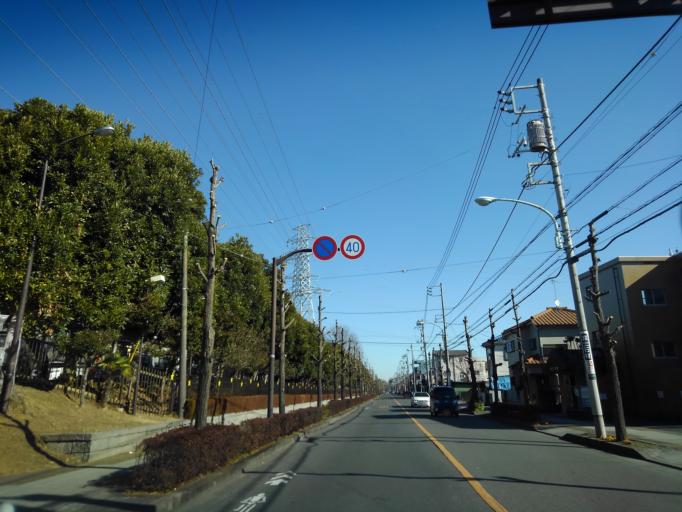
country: JP
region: Tokyo
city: Fussa
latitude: 35.7655
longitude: 139.3214
